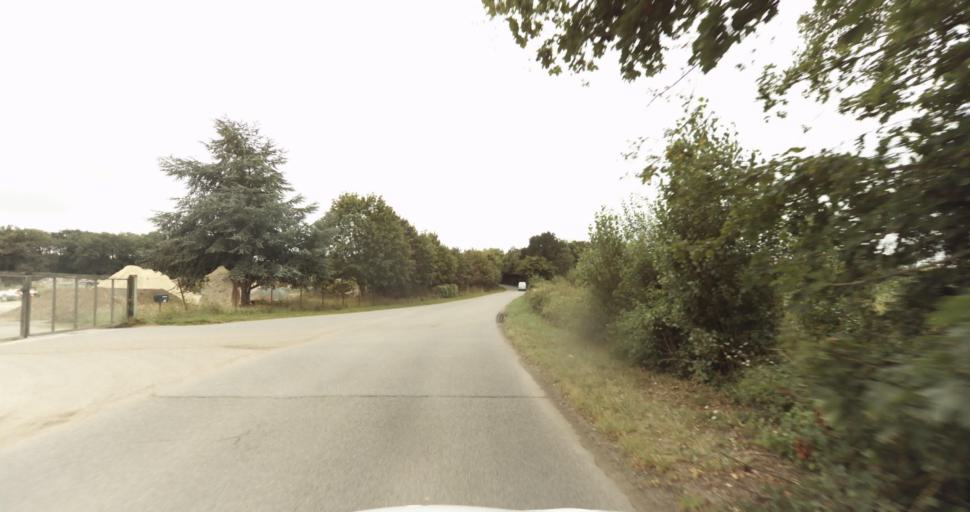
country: FR
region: Haute-Normandie
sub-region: Departement de l'Eure
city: Gravigny
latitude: 49.0399
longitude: 1.1740
